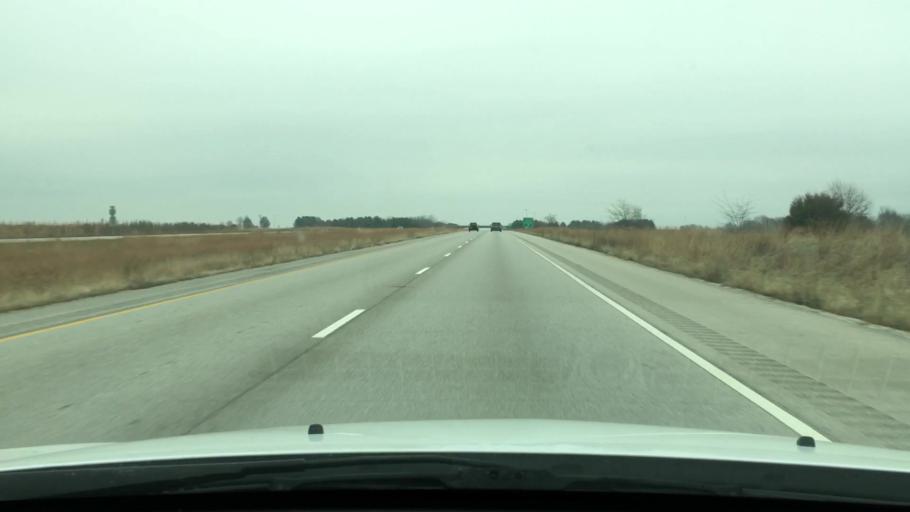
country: US
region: Illinois
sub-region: Sangamon County
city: New Berlin
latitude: 39.7368
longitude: -90.0533
